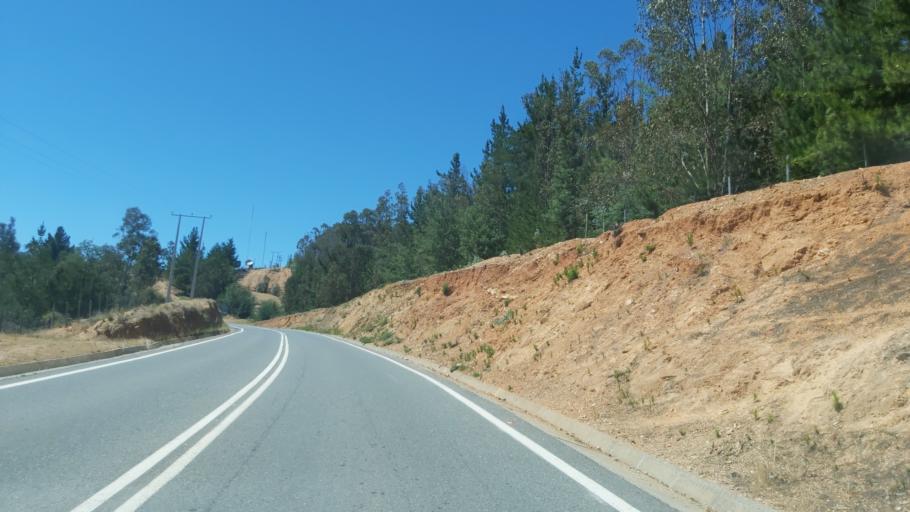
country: CL
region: Maule
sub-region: Provincia de Talca
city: Constitucion
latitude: -34.9140
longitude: -71.9955
